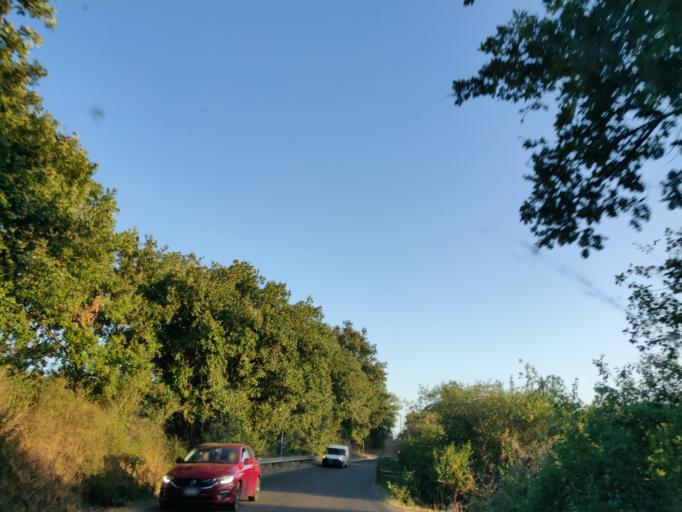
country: IT
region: Latium
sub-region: Provincia di Viterbo
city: Canino
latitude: 42.4223
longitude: 11.7078
